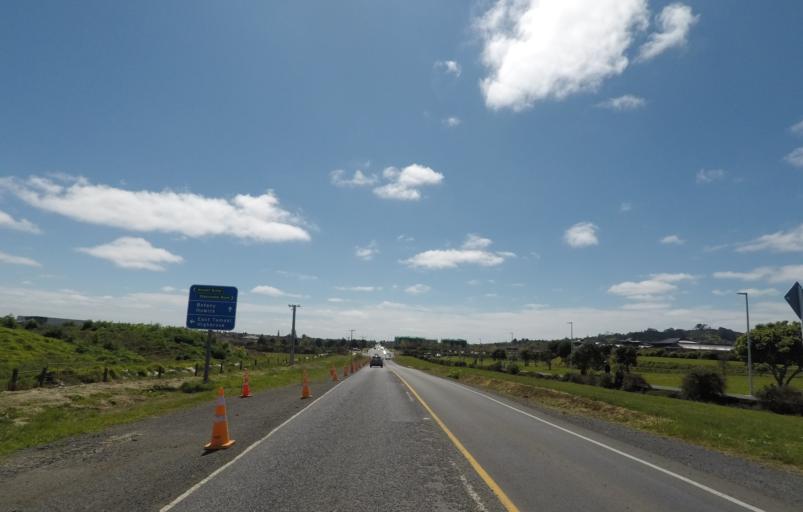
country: NZ
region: Auckland
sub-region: Auckland
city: Manukau City
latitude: -36.9598
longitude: 174.9080
